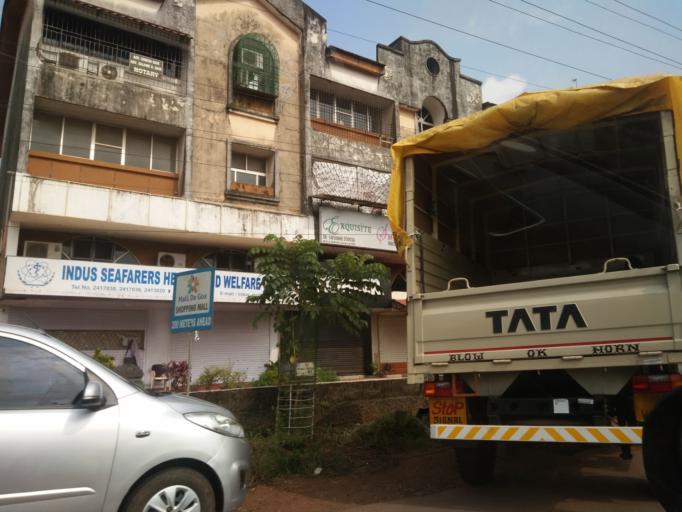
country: IN
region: Goa
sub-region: North Goa
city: Serula
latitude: 15.5275
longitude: 73.8262
